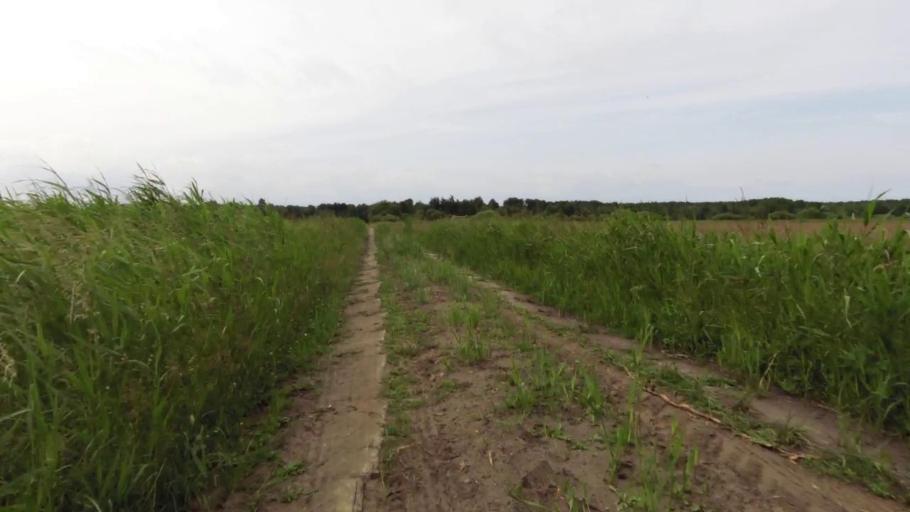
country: PL
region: West Pomeranian Voivodeship
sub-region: Powiat goleniowski
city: Stepnica
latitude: 53.7391
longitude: 14.6072
